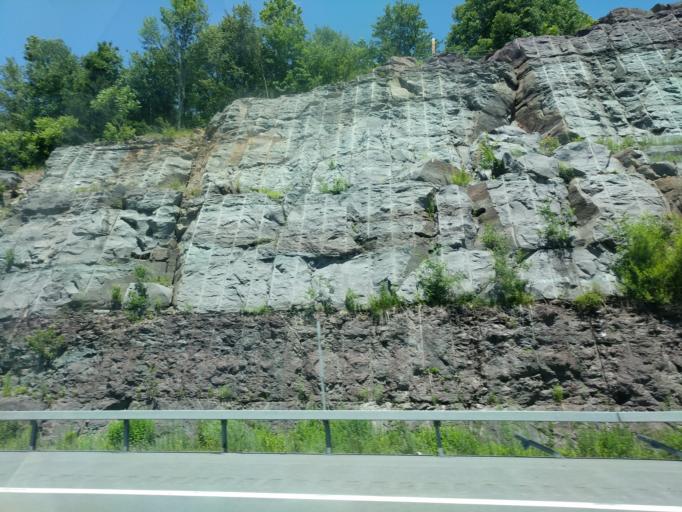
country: US
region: New York
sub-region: Sullivan County
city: Rock Hill
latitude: 41.6355
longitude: -74.6155
